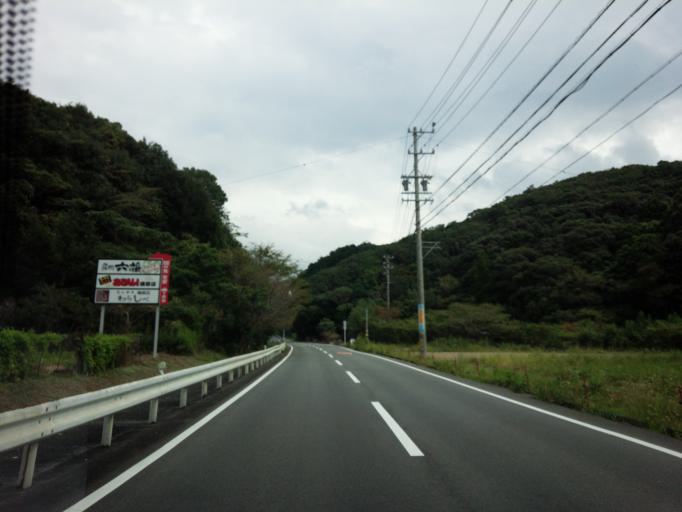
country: JP
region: Mie
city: Toba
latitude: 34.3153
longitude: 136.7788
